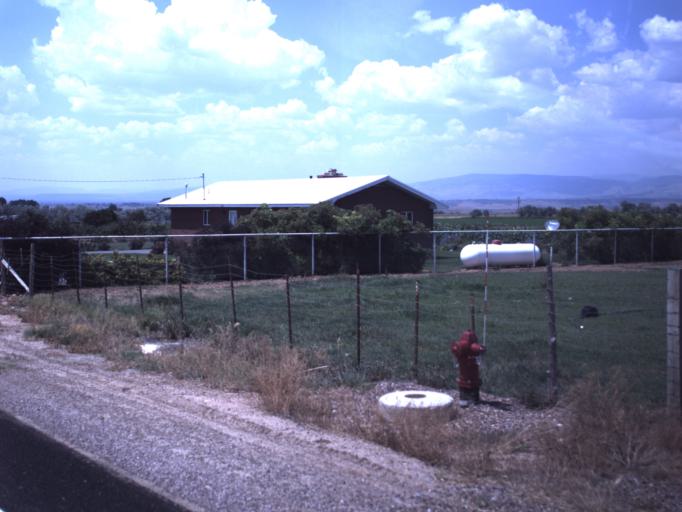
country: US
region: Utah
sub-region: Duchesne County
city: Roosevelt
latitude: 40.4037
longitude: -109.8033
